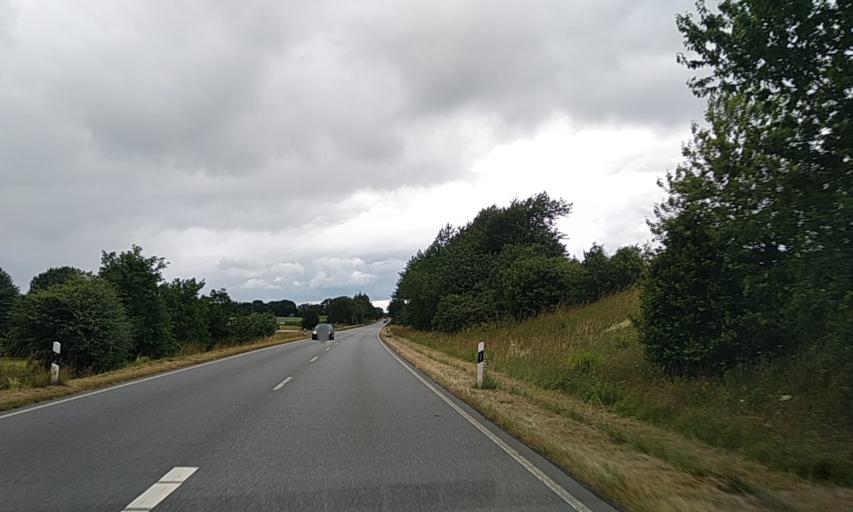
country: DE
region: Schleswig-Holstein
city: Schleswig
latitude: 54.5399
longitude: 9.5516
